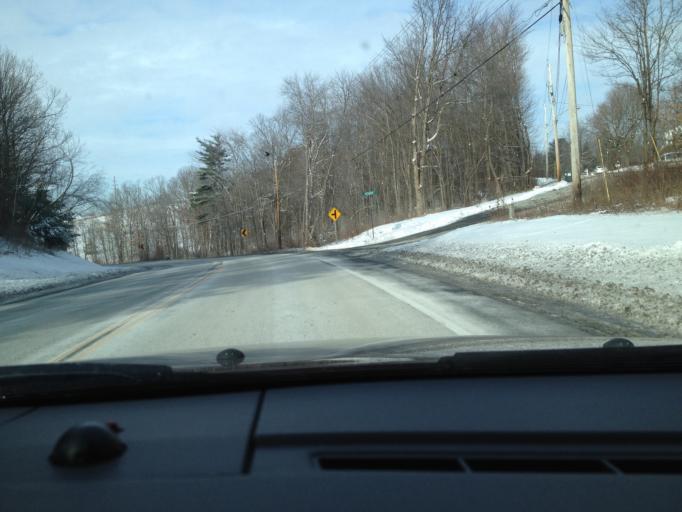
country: US
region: New York
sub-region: Rensselaer County
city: West Sand Lake
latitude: 42.6415
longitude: -73.6170
